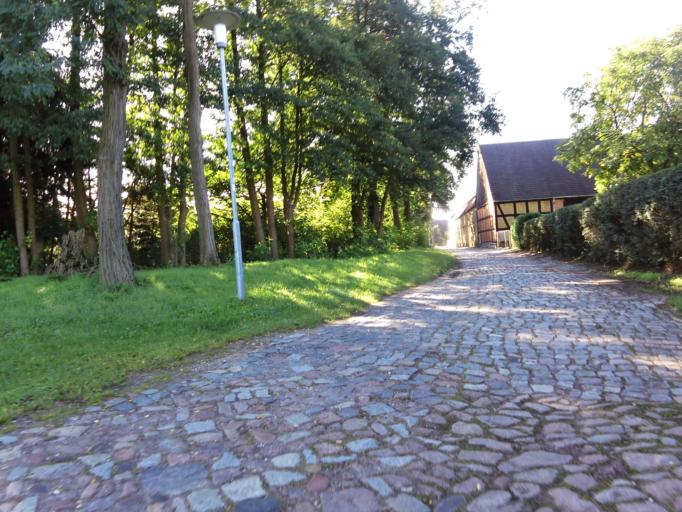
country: DE
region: Saxony-Anhalt
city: Coswig
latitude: 51.8826
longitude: 12.5072
